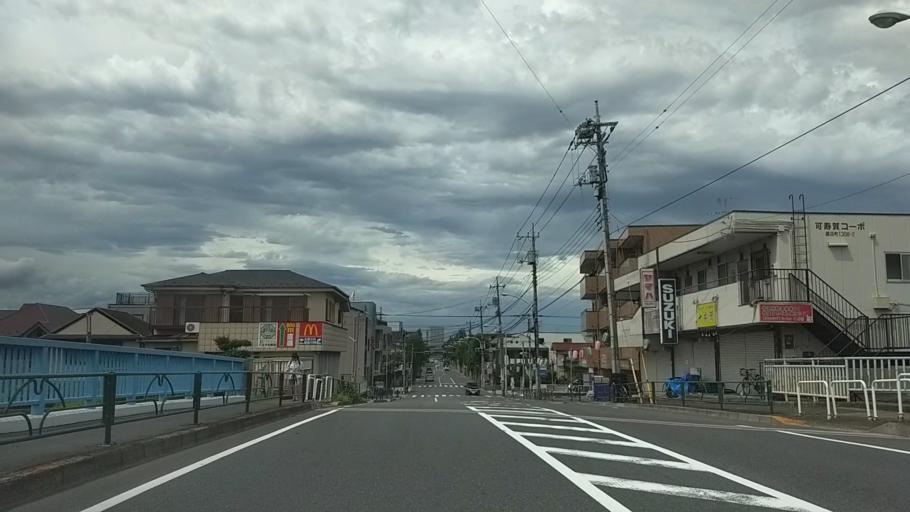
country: JP
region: Tokyo
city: Hachioji
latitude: 35.6447
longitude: 139.3609
